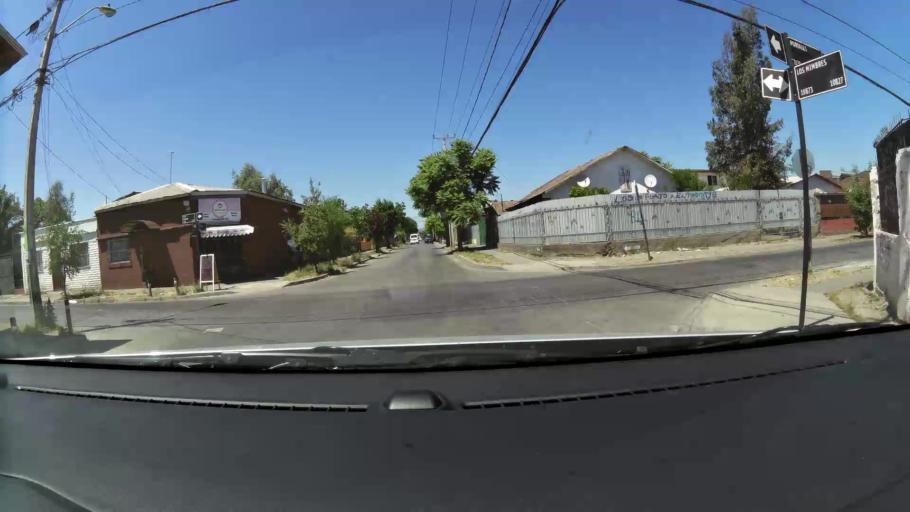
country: CL
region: Santiago Metropolitan
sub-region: Provincia de Santiago
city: La Pintana
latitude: -33.5625
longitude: -70.6624
